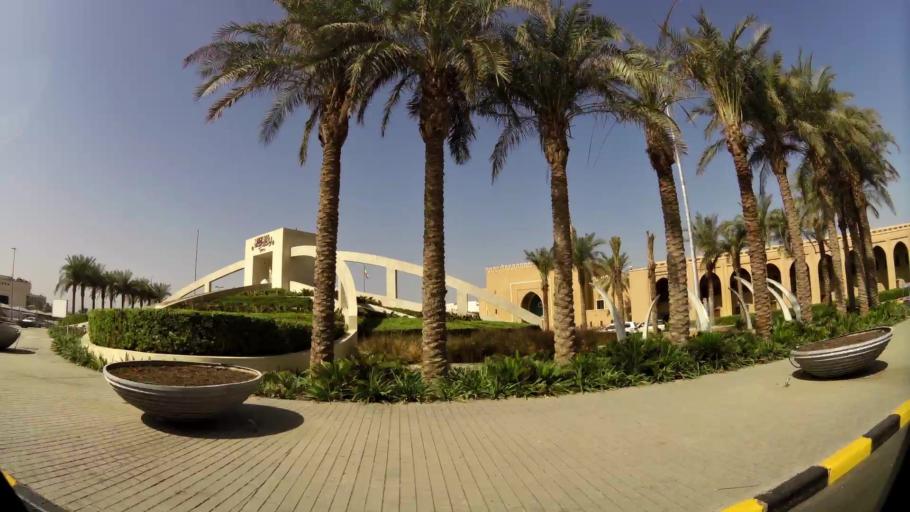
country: KW
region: Al Asimah
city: Kuwait City
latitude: 29.3798
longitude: 47.9739
